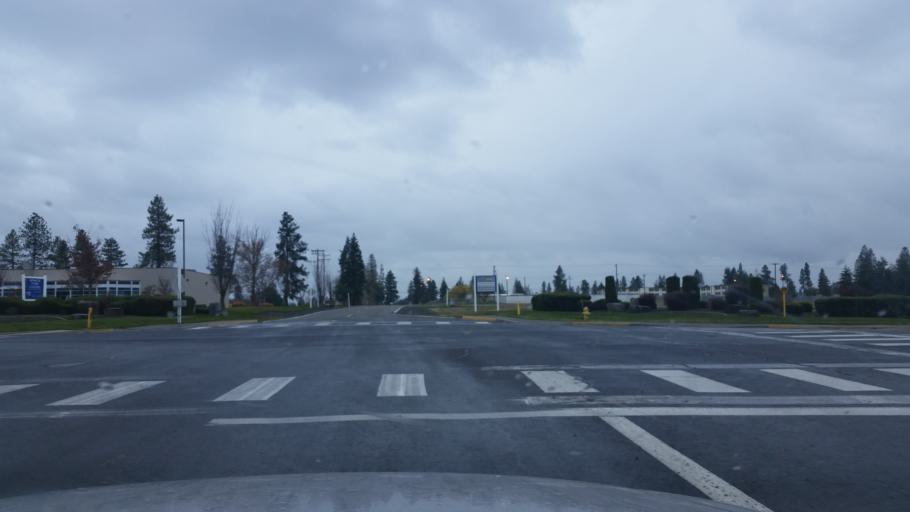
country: US
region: Washington
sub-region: Spokane County
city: Airway Heights
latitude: 47.6256
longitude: -117.5133
